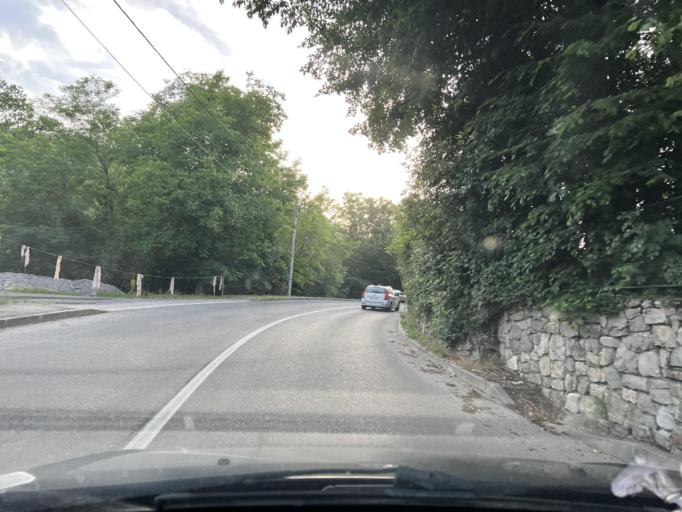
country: HR
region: Primorsko-Goranska
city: Marcelji
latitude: 45.3945
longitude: 14.4273
